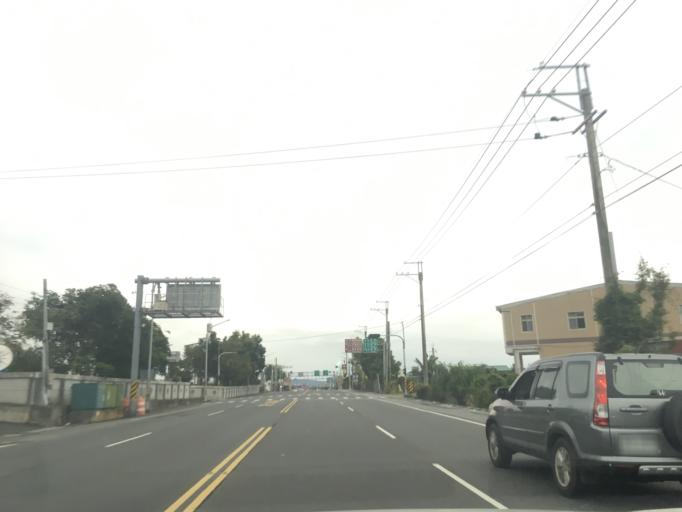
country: TW
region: Taiwan
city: Taitung City
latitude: 22.6870
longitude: 121.0449
